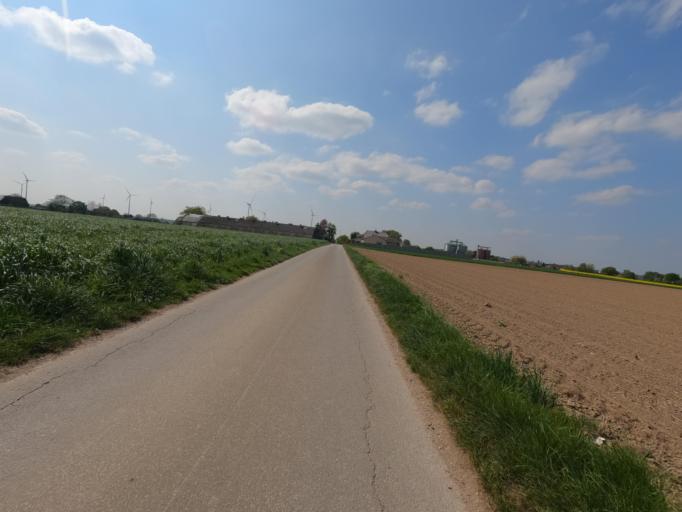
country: DE
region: North Rhine-Westphalia
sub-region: Regierungsbezirk Koln
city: Heinsberg
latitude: 51.0472
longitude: 6.0438
